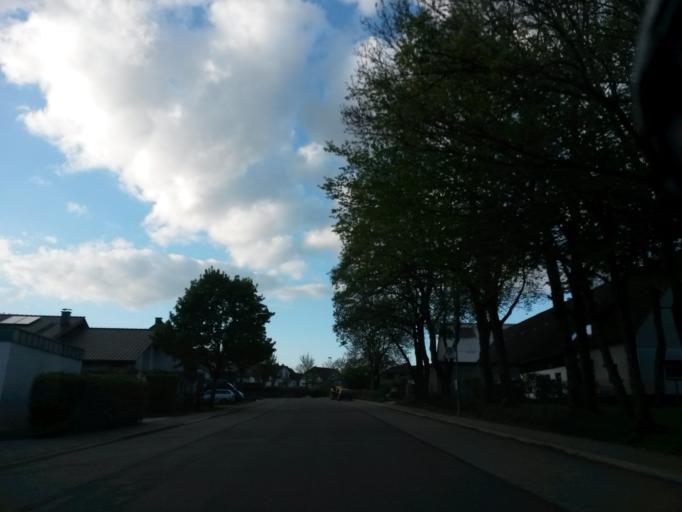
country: DE
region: North Rhine-Westphalia
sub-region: Regierungsbezirk Arnsberg
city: Herscheid
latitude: 51.1805
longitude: 7.7507
